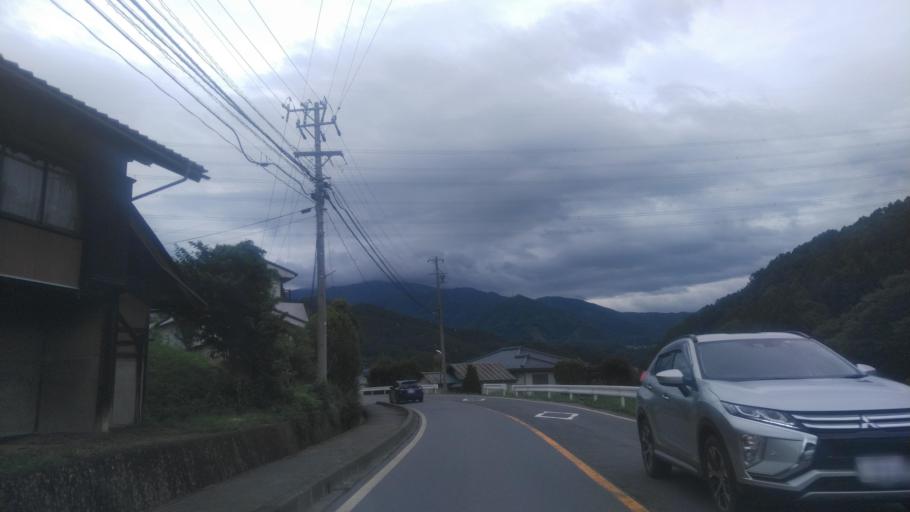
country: JP
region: Nagano
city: Ueda
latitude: 36.4580
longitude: 138.2822
